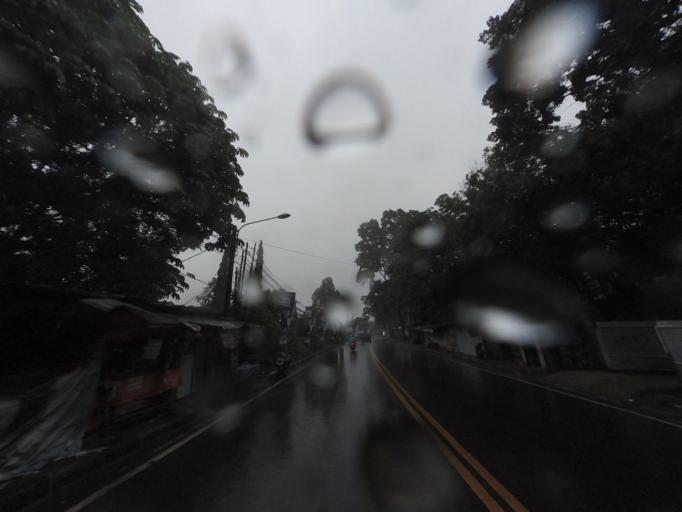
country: ID
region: West Java
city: Caringin
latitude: -6.6598
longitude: 106.8570
